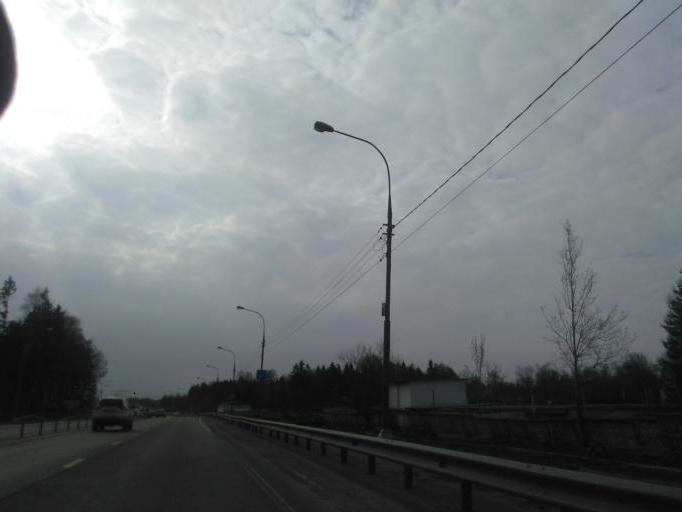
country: RU
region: Moskovskaya
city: Yermolino
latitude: 56.1287
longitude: 37.5113
